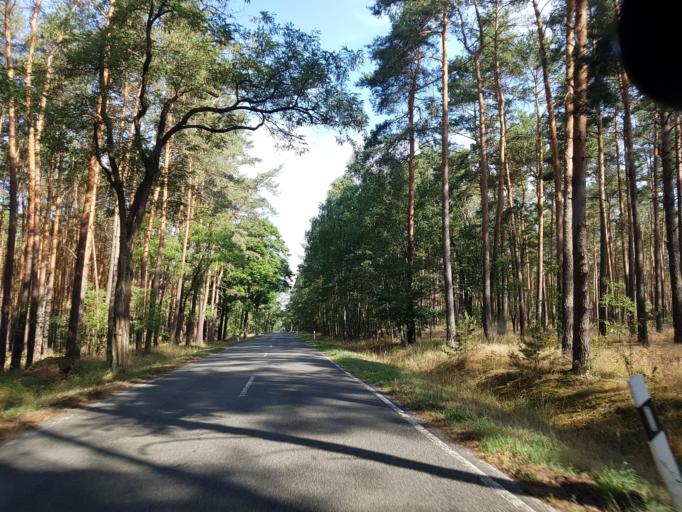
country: DE
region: Brandenburg
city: Ihlow
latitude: 51.9694
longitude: 13.3137
